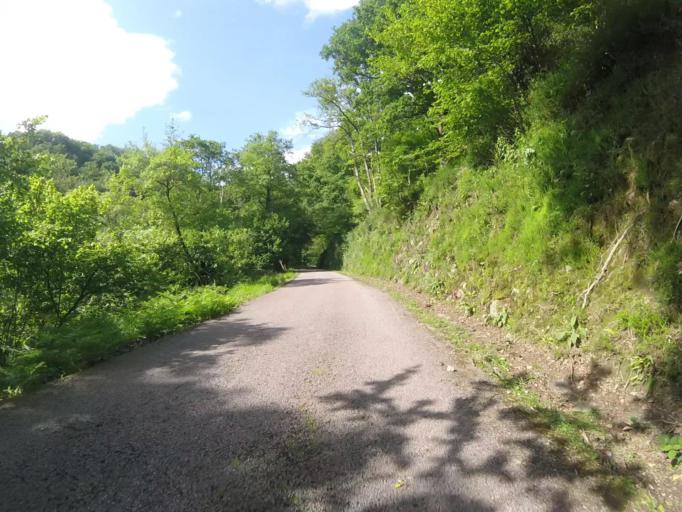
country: ES
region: Navarre
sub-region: Provincia de Navarra
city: Goizueta
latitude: 43.2183
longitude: -1.8059
